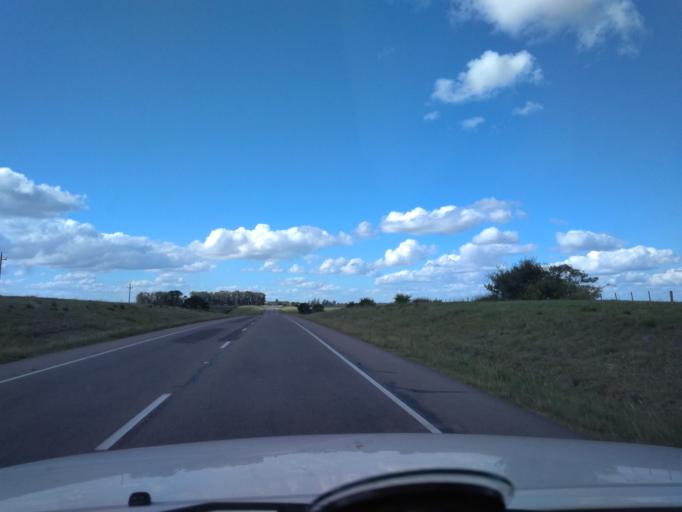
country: UY
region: Florida
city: Cardal
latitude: -34.3054
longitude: -56.2327
